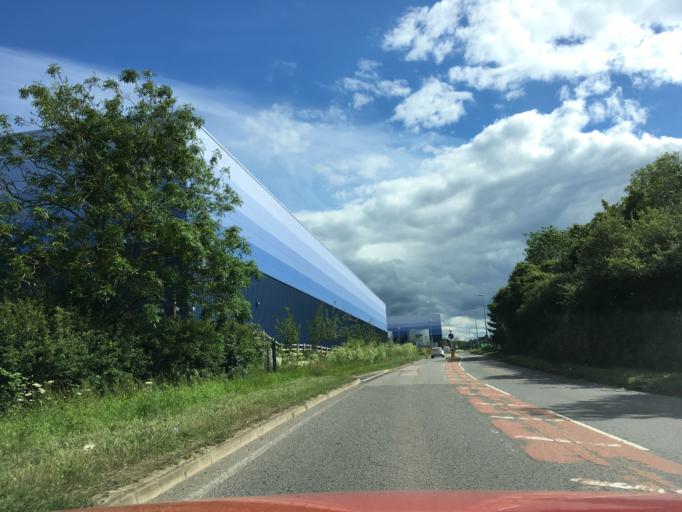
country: GB
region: England
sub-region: Milton Keynes
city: Wavendon
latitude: 52.0388
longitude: -0.6760
